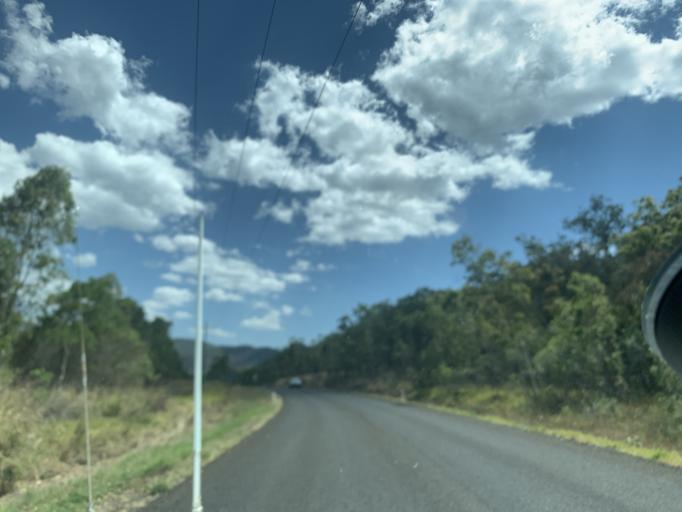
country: AU
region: Queensland
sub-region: Tablelands
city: Atherton
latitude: -17.3053
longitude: 145.4583
